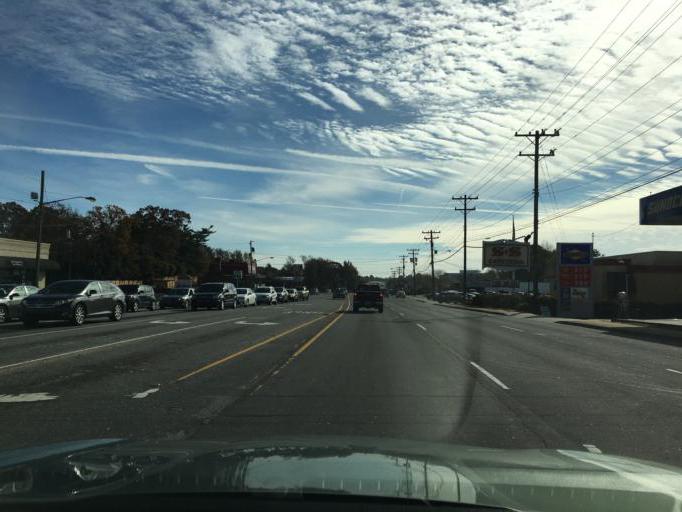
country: US
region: South Carolina
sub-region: Greenville County
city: Greenville
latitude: 34.8687
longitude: -82.3583
